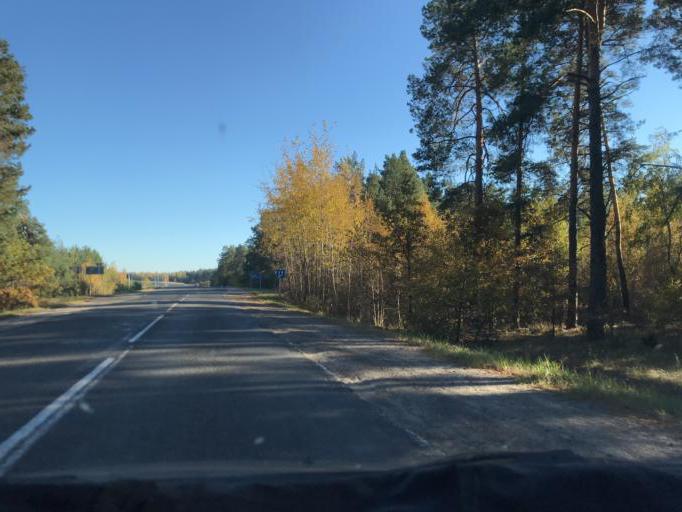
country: BY
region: Gomel
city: Kalinkavichy
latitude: 52.0762
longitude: 29.3547
